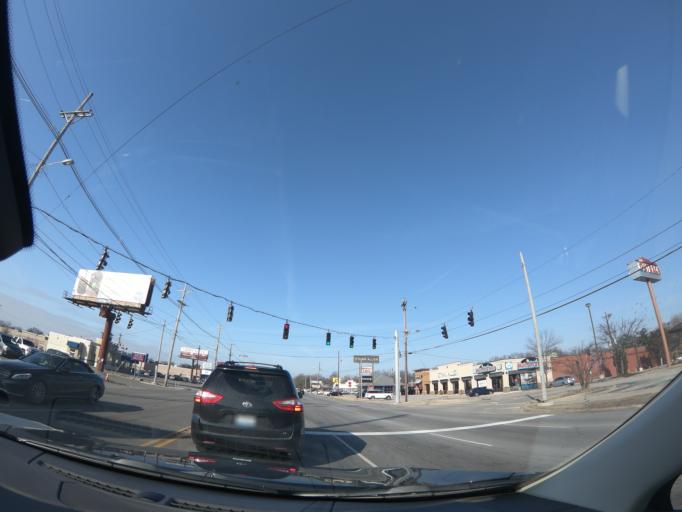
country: US
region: Kentucky
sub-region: Jefferson County
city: Beechwood Village
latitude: 38.2506
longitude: -85.6267
